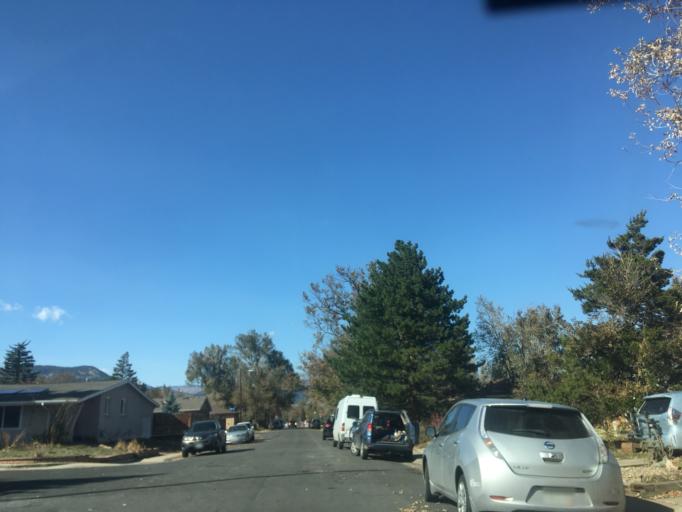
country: US
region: Colorado
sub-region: Boulder County
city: Boulder
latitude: 39.9896
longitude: -105.2458
